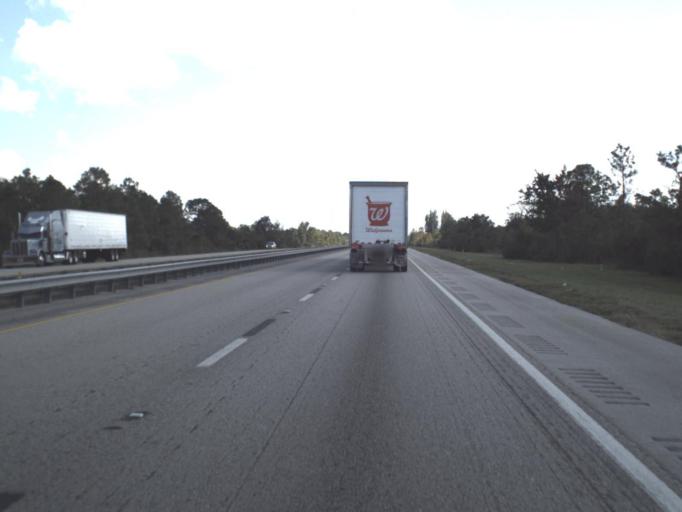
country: US
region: Florida
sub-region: Indian River County
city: Fellsmere
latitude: 27.7382
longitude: -80.9247
